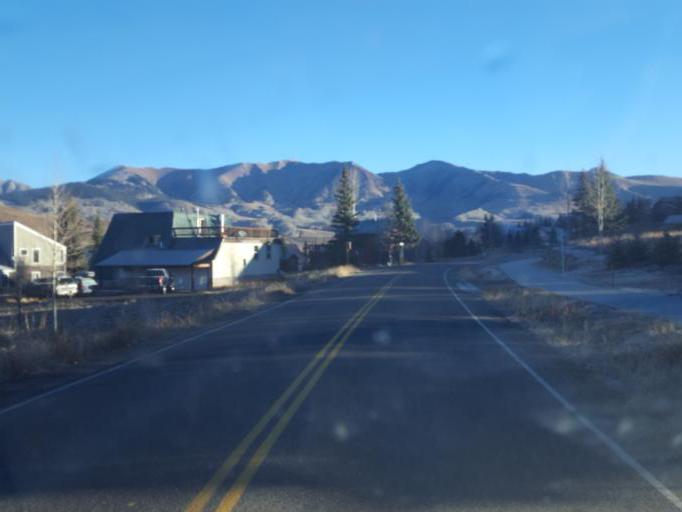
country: US
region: Colorado
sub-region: Gunnison County
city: Crested Butte
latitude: 38.9080
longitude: -106.9703
